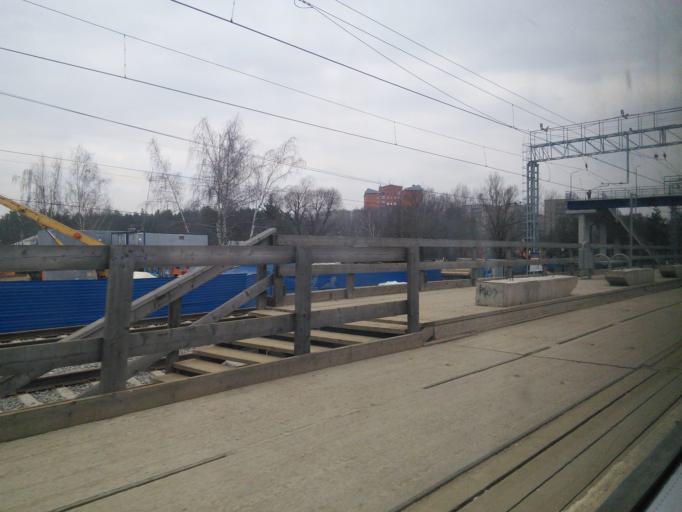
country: RU
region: Moskovskaya
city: Vostryakovo
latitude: 55.4223
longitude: 37.8365
